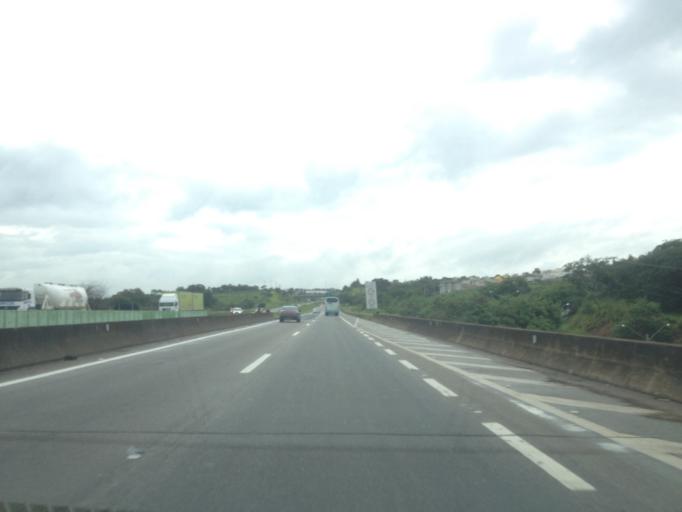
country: BR
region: Sao Paulo
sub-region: Itu
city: Itu
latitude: -23.2720
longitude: -47.3261
